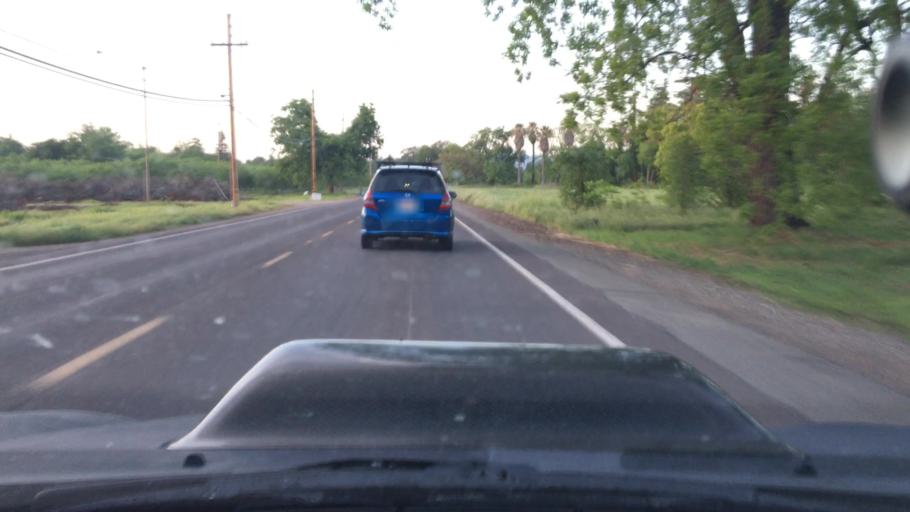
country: US
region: California
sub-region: Butte County
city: Chico
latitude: 39.7108
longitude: -121.8453
